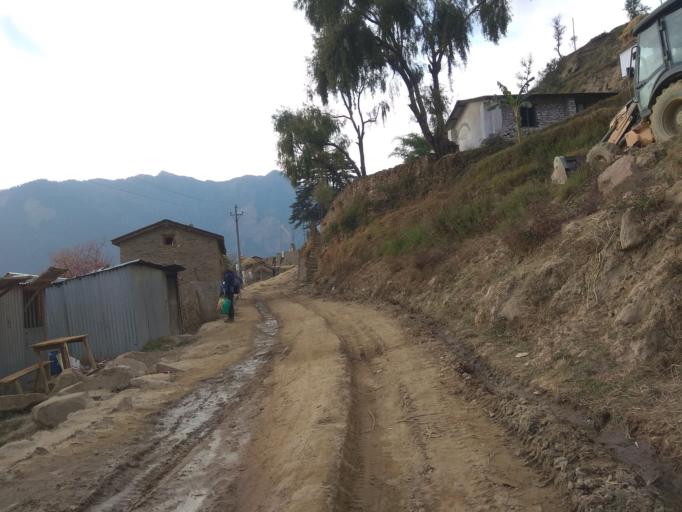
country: NP
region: Far Western
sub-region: Seti Zone
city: Achham
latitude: 29.2540
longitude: 81.6362
